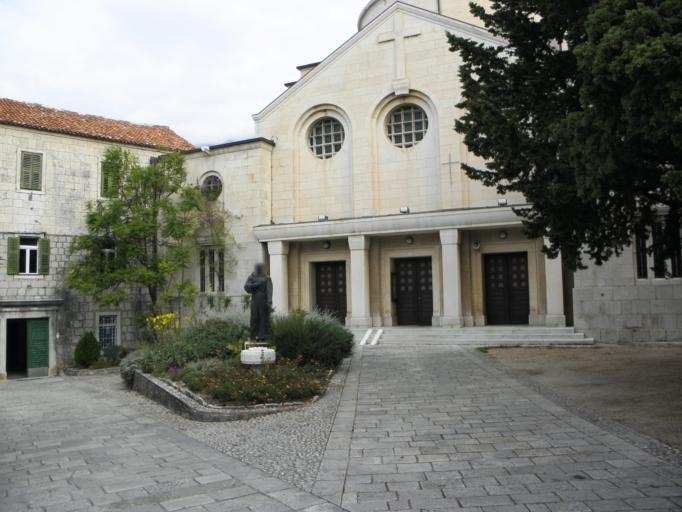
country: HR
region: Splitsko-Dalmatinska
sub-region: Grad Makarska
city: Makarska
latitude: 43.2915
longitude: 17.0207
